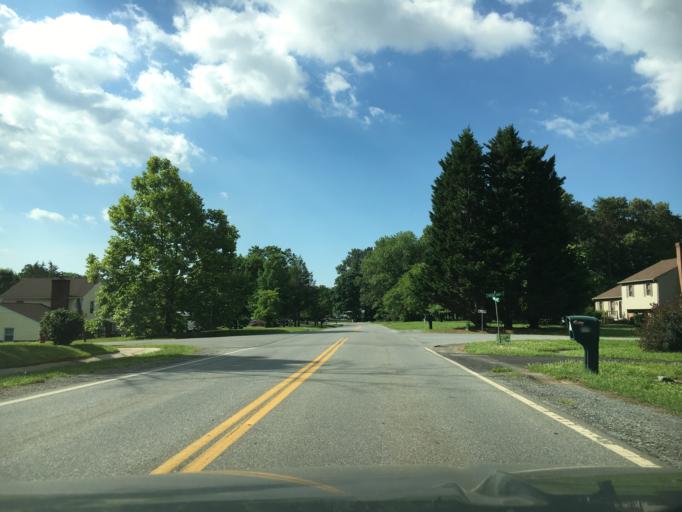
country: US
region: Virginia
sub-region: Bedford County
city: Forest
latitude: 37.3930
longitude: -79.2482
